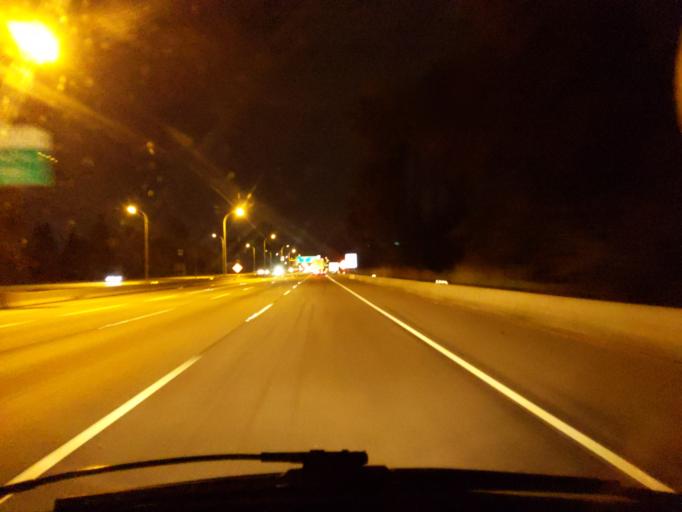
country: CA
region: British Columbia
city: Walnut Grove
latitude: 49.1679
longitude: -122.6839
